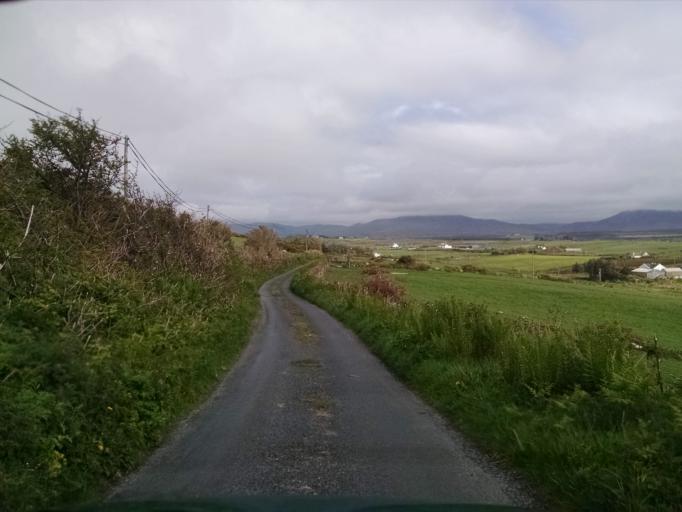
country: IE
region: Connaught
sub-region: County Galway
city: Clifden
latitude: 53.7607
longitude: -9.8496
